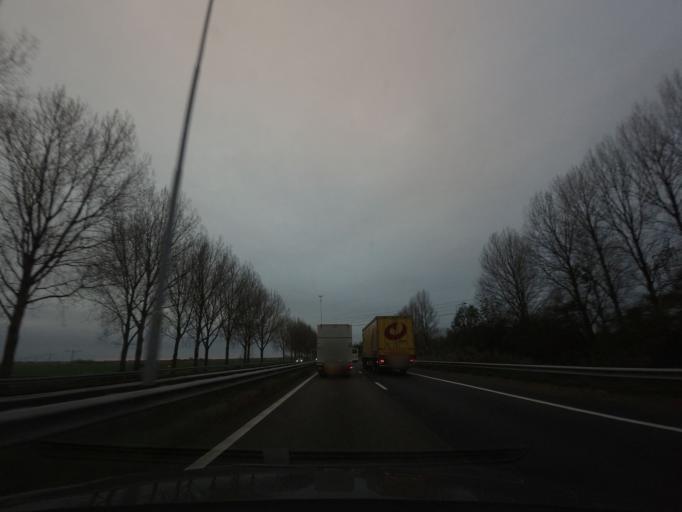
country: NL
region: North Brabant
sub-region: Gemeente Oosterhout
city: Oosterhout
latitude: 51.6674
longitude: 4.8800
